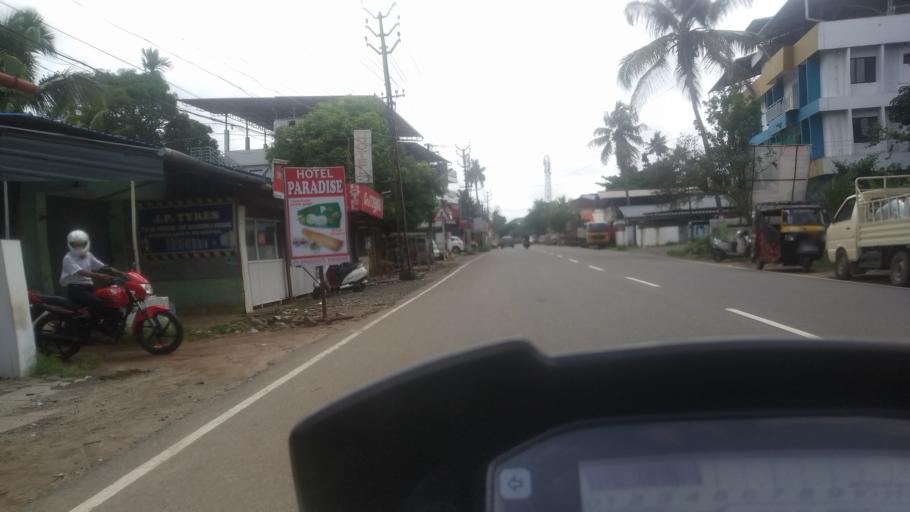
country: IN
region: Kerala
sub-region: Ernakulam
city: Aluva
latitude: 10.1271
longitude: 76.3107
